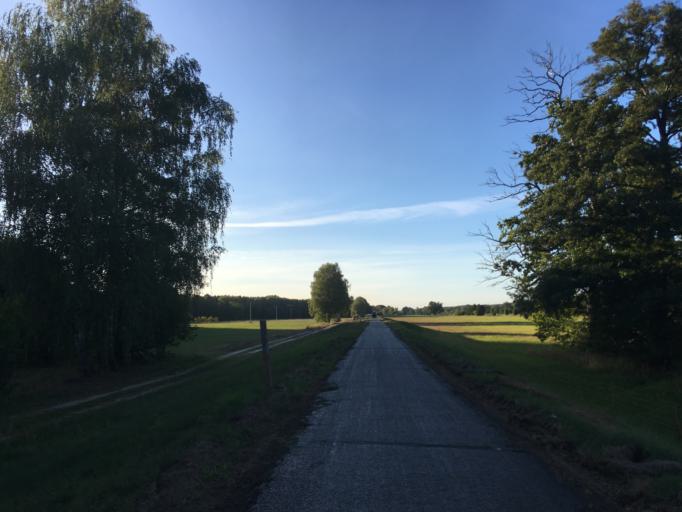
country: DE
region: Brandenburg
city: Forst
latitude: 51.6954
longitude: 14.7153
